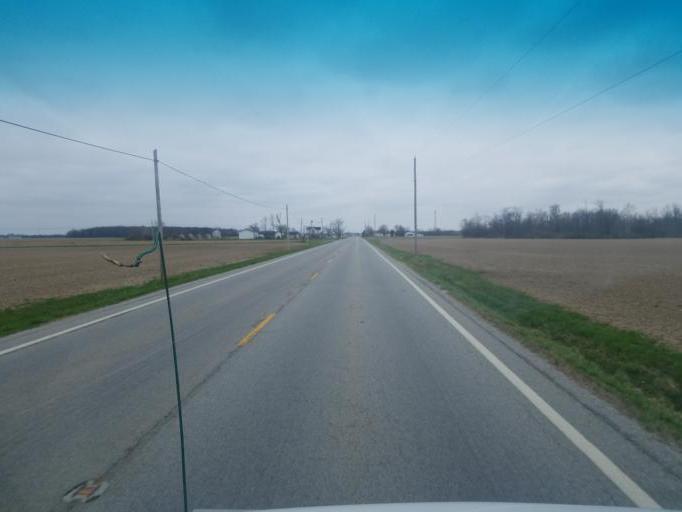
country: US
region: Ohio
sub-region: Van Wert County
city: Van Wert
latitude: 40.9112
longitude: -84.5590
